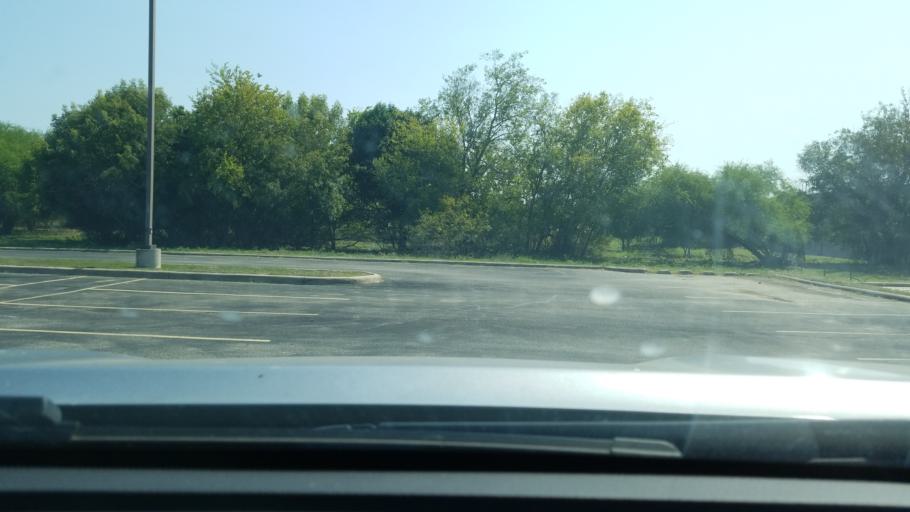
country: US
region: Texas
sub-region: Bexar County
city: Leon Valley
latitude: 29.5470
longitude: -98.6140
